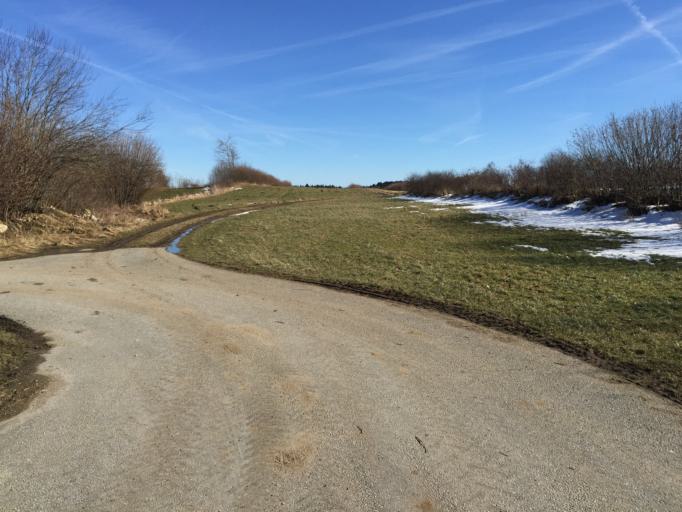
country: AT
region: Lower Austria
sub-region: Politischer Bezirk Gmund
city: Weitra
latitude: 48.6657
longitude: 14.9364
